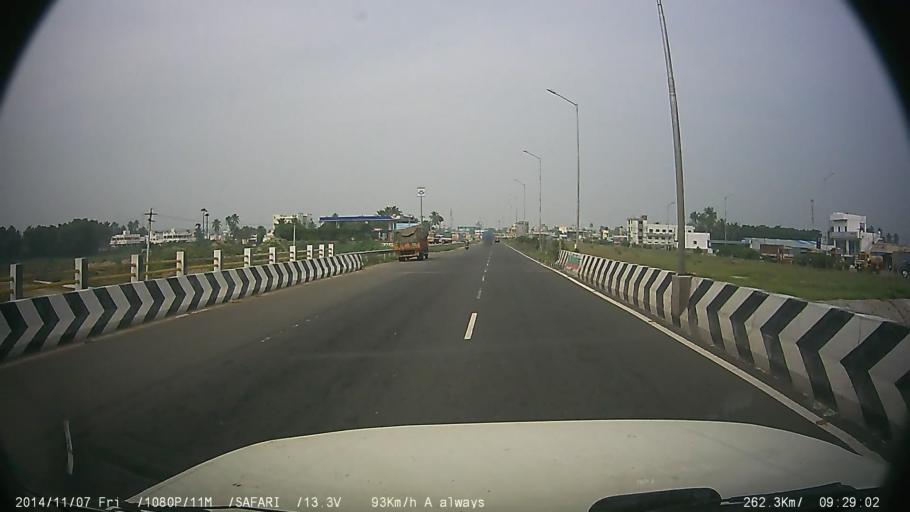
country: IN
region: Tamil Nadu
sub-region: Erode
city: Bhavani
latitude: 11.4315
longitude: 77.6822
